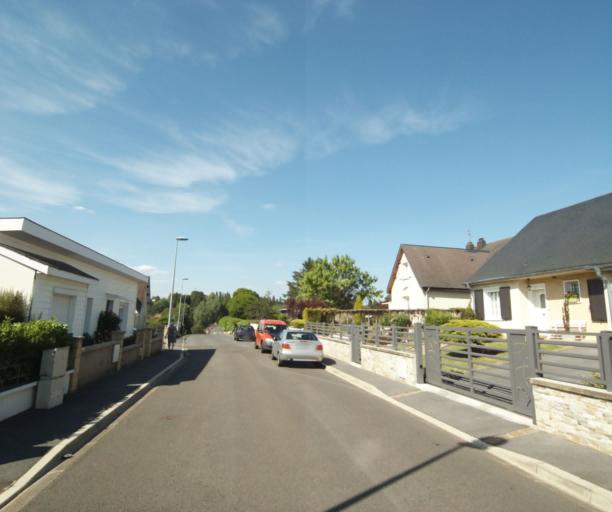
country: FR
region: Champagne-Ardenne
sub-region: Departement des Ardennes
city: Warcq
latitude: 49.7804
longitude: 4.6992
